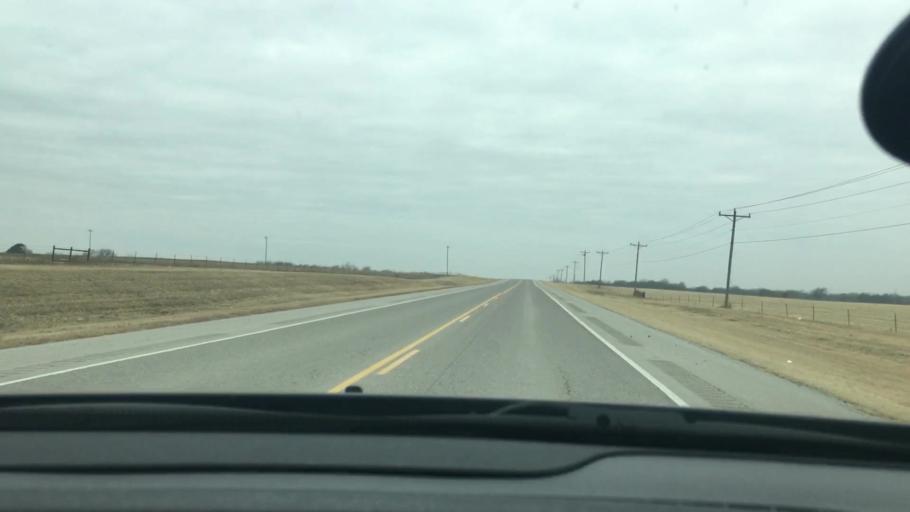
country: US
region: Oklahoma
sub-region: Murray County
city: Davis
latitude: 34.5213
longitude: -97.2938
